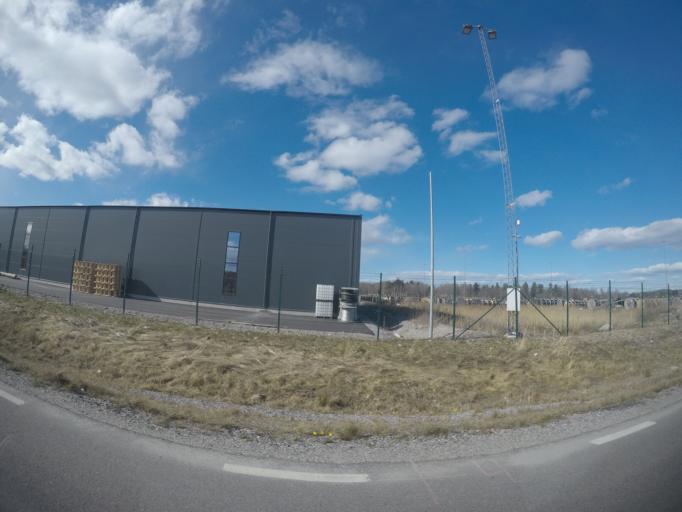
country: SE
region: OErebro
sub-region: Orebro Kommun
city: Hovsta
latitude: 59.3042
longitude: 15.2708
